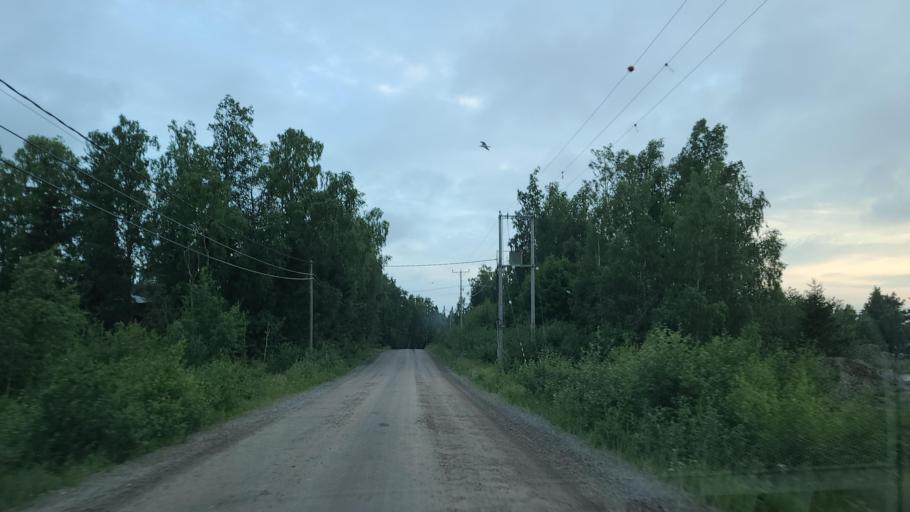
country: FI
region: Ostrobothnia
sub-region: Vaasa
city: Replot
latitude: 63.2962
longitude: 21.1202
